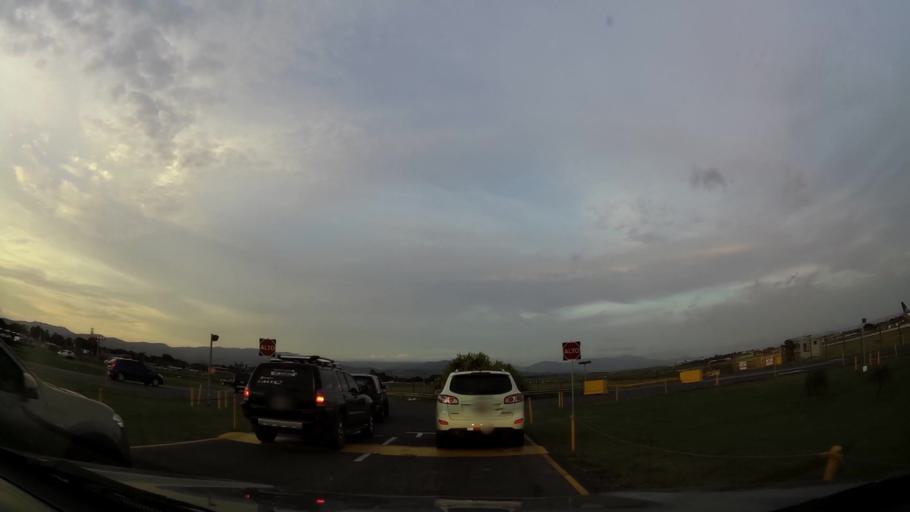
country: PA
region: Panama
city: Tocumen
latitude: 9.0710
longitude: -79.3879
